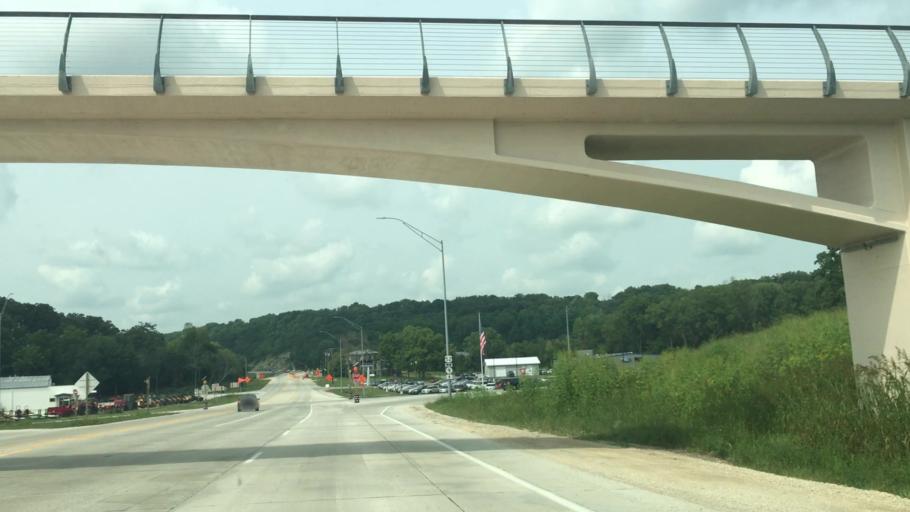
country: US
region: Iowa
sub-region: Winneshiek County
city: Decorah
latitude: 43.2918
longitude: -91.8038
